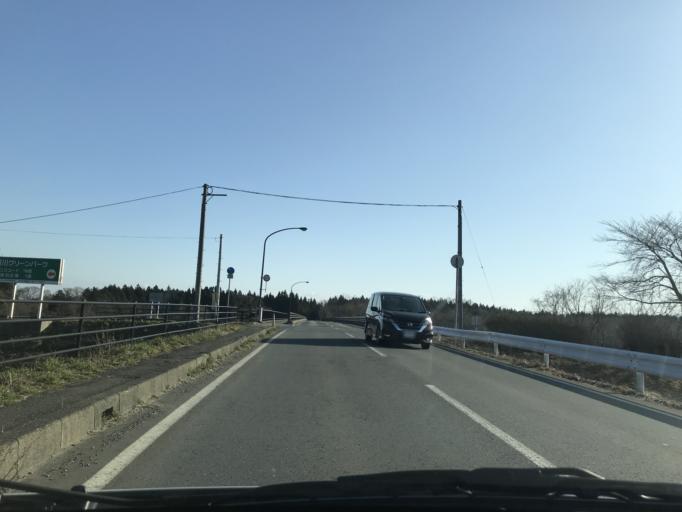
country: JP
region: Iwate
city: Kitakami
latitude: 39.2922
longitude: 141.0691
